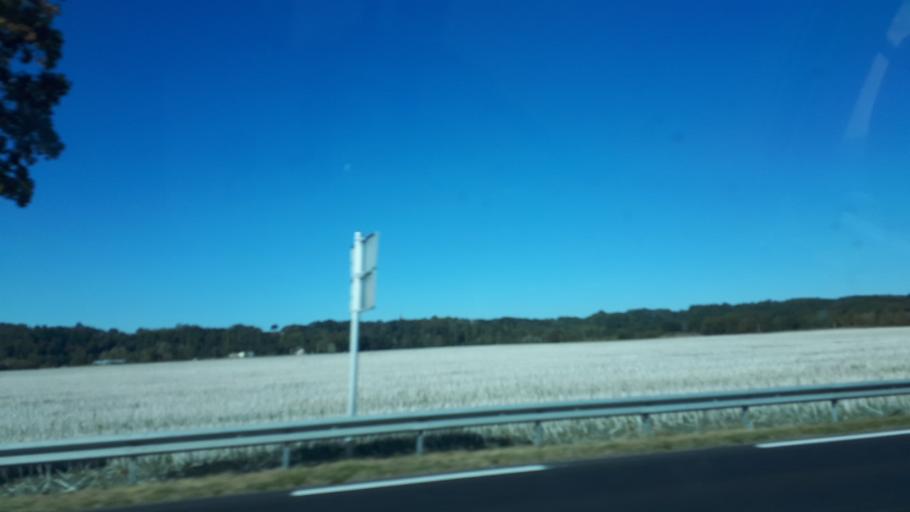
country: FR
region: Centre
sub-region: Departement d'Eure-et-Loir
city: Marboue
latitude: 48.1039
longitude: 1.3300
